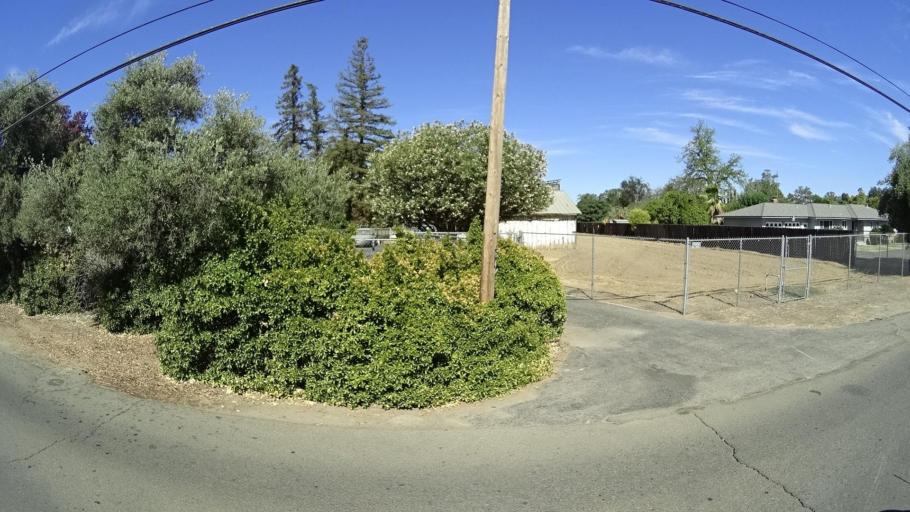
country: US
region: California
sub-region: Fresno County
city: Sunnyside
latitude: 36.7371
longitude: -119.7093
